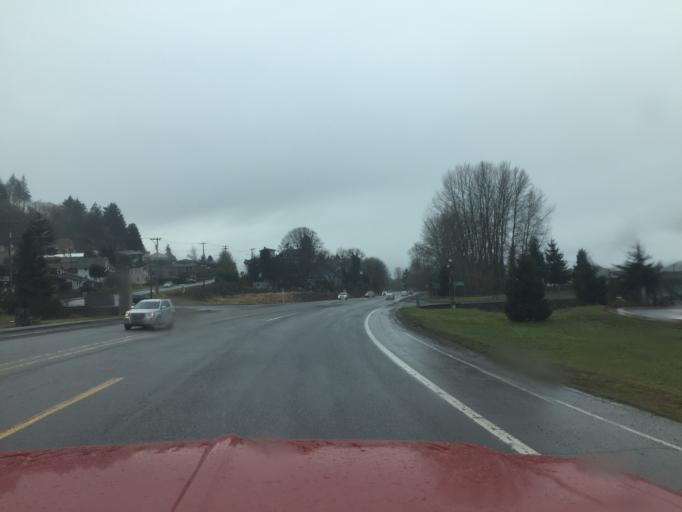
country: US
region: Oregon
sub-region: Columbia County
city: Rainier
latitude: 46.0904
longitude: -122.9421
